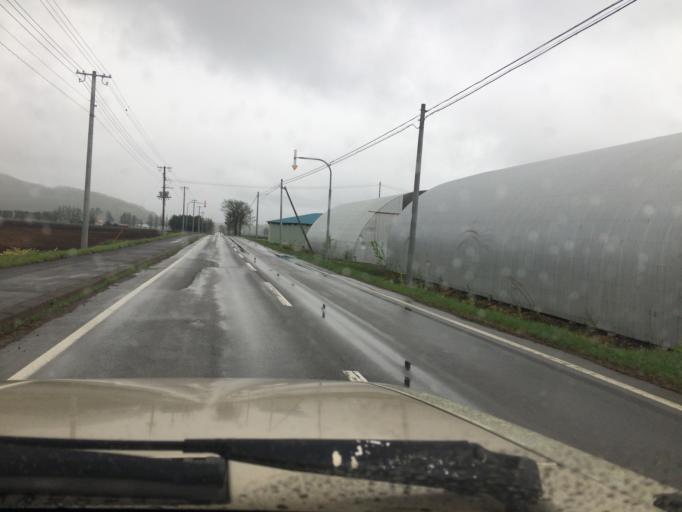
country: JP
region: Hokkaido
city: Obihiro
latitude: 42.8109
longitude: 142.9669
